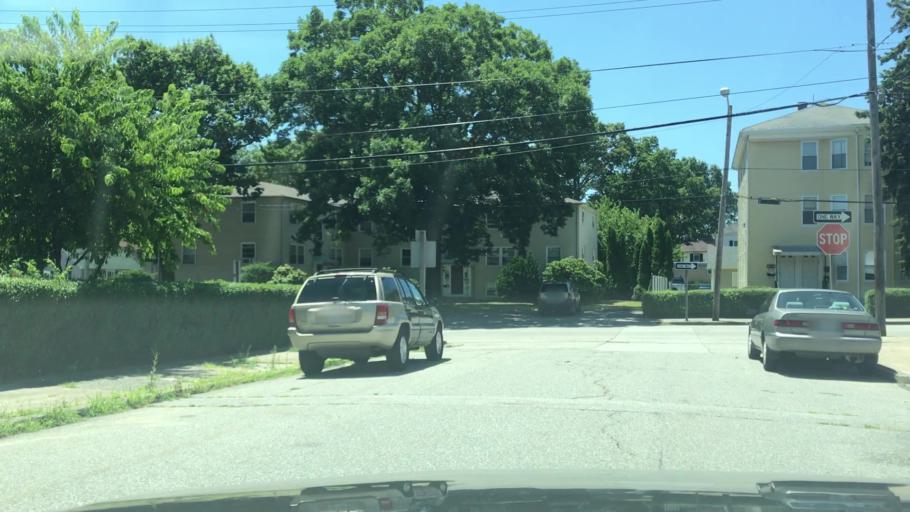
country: US
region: Rhode Island
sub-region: Providence County
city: Pawtucket
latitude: 41.8649
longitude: -71.3723
